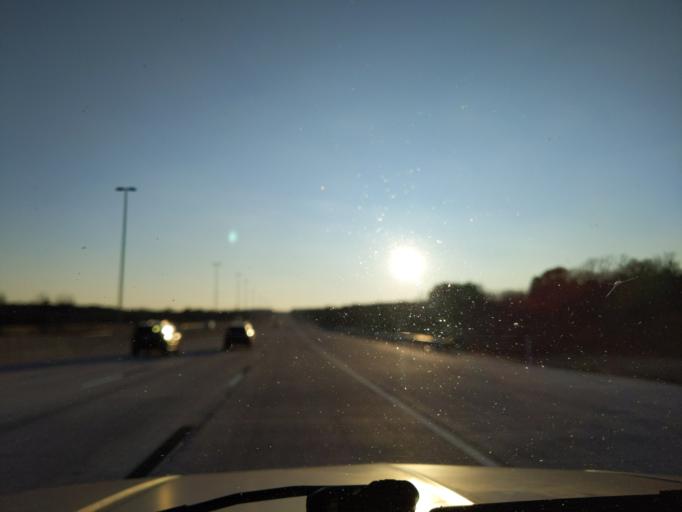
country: US
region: Oklahoma
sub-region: Creek County
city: Kellyville
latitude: 35.9238
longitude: -96.2817
